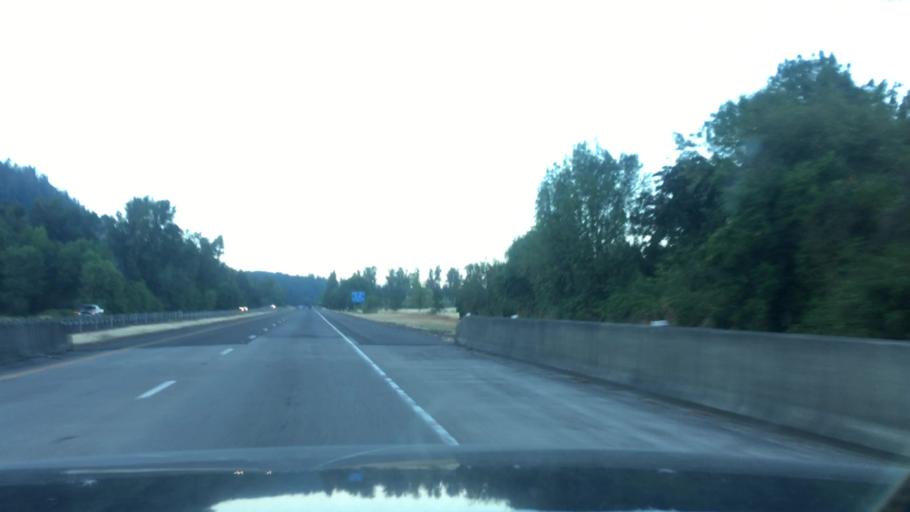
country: US
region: Oregon
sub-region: Lane County
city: Creswell
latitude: 43.8840
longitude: -123.0140
